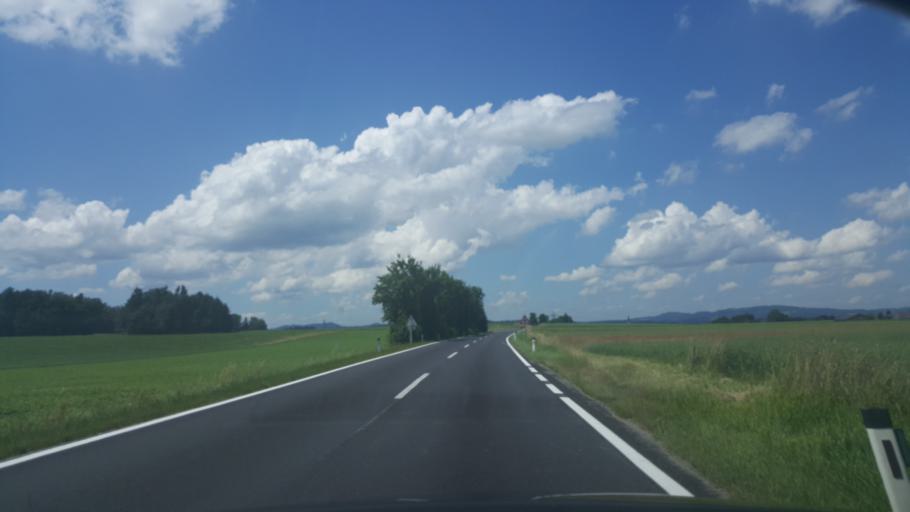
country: AT
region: Upper Austria
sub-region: Politischer Bezirk Vocklabruck
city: Gampern
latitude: 47.9703
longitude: 13.5660
